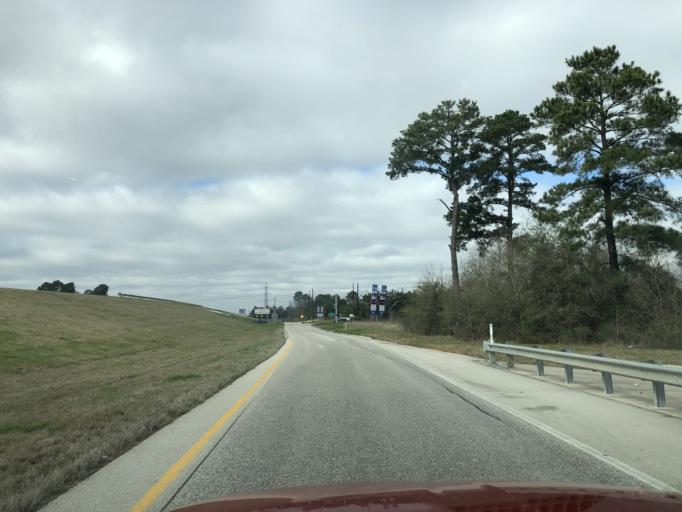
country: US
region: Texas
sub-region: Montgomery County
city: The Woodlands
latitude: 30.0949
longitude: -95.5047
